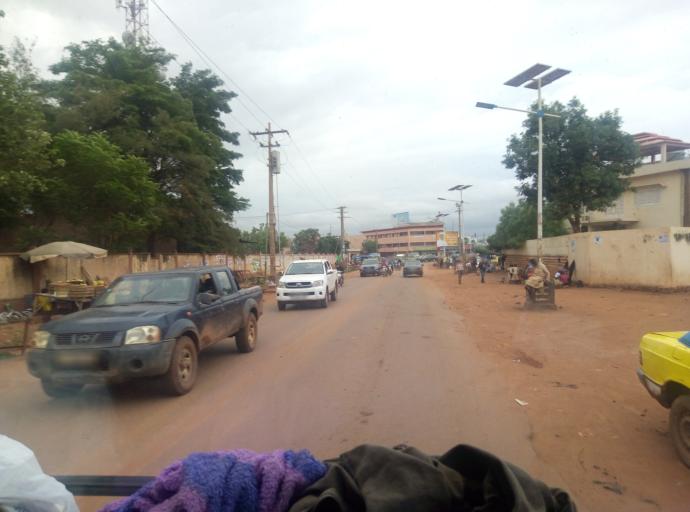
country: ML
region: Bamako
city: Bamako
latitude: 12.6021
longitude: -7.9642
